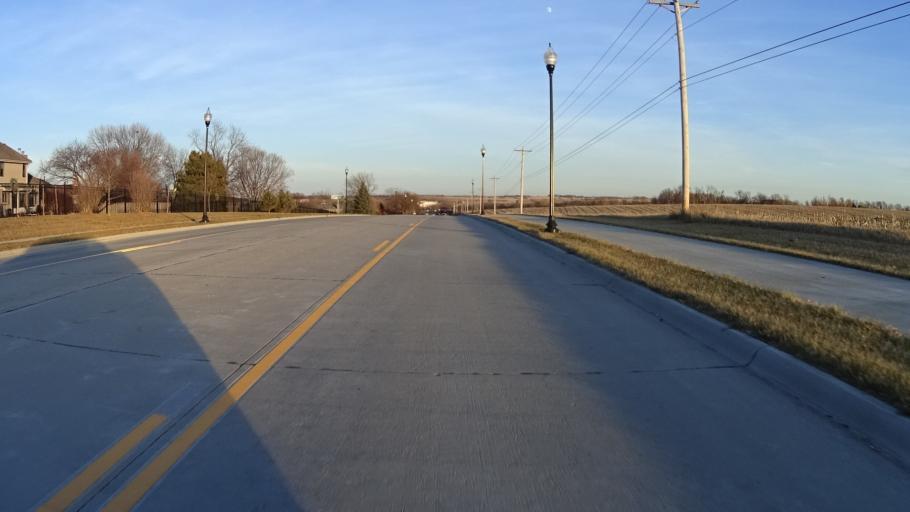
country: US
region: Nebraska
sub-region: Sarpy County
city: Papillion
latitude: 41.1326
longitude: -96.0493
